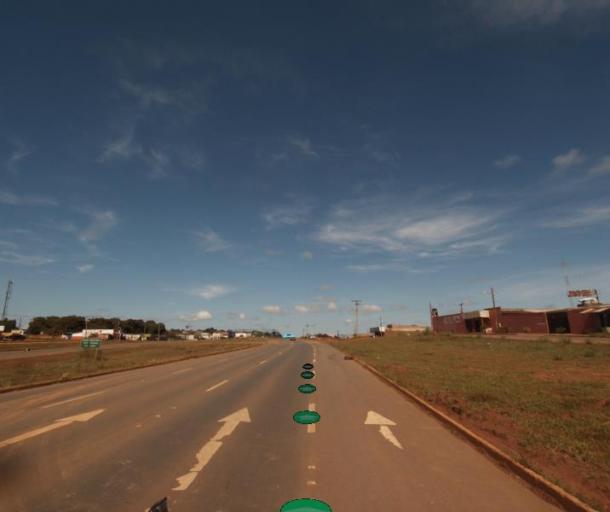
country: BR
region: Federal District
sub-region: Brasilia
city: Brasilia
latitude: -15.7509
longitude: -48.3248
